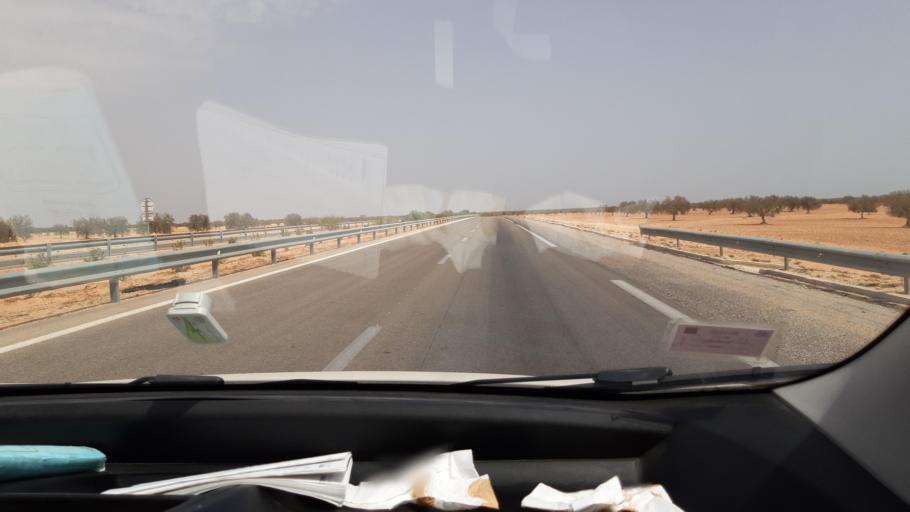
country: TN
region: Safaqis
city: Bi'r `Ali Bin Khalifah
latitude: 34.5669
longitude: 10.3647
